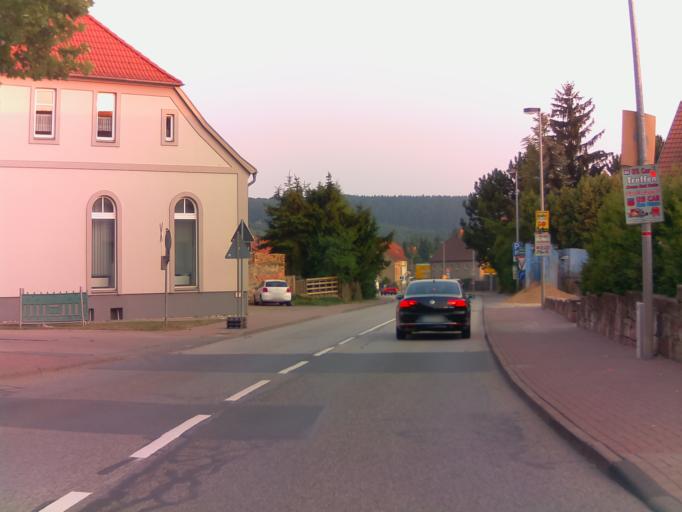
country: DE
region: Thuringia
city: Bad Berka
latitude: 50.9022
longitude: 11.2804
